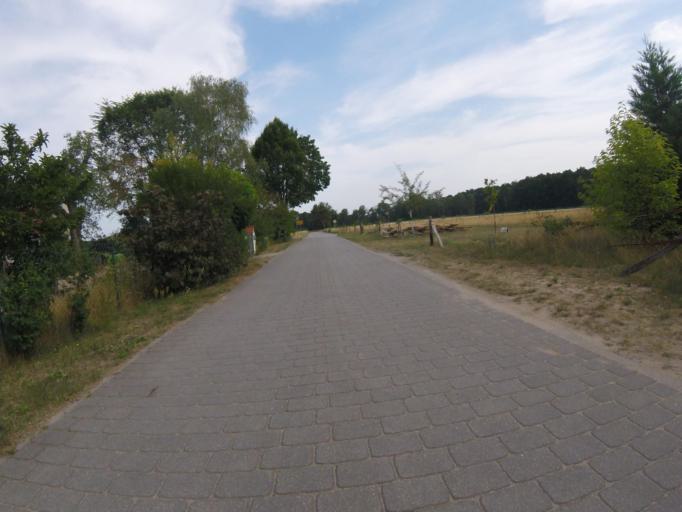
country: DE
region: Brandenburg
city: Erkner
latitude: 52.3127
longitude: 13.7521
